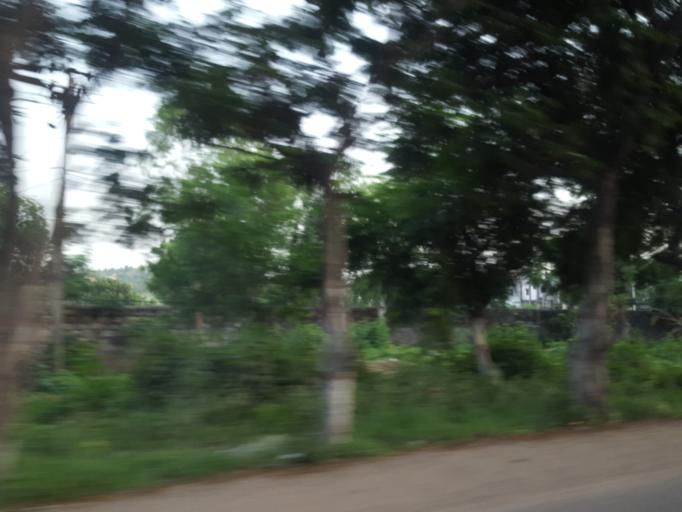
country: IN
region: Telangana
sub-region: Rangareddi
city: Kukatpalli
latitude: 17.5426
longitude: 78.3702
